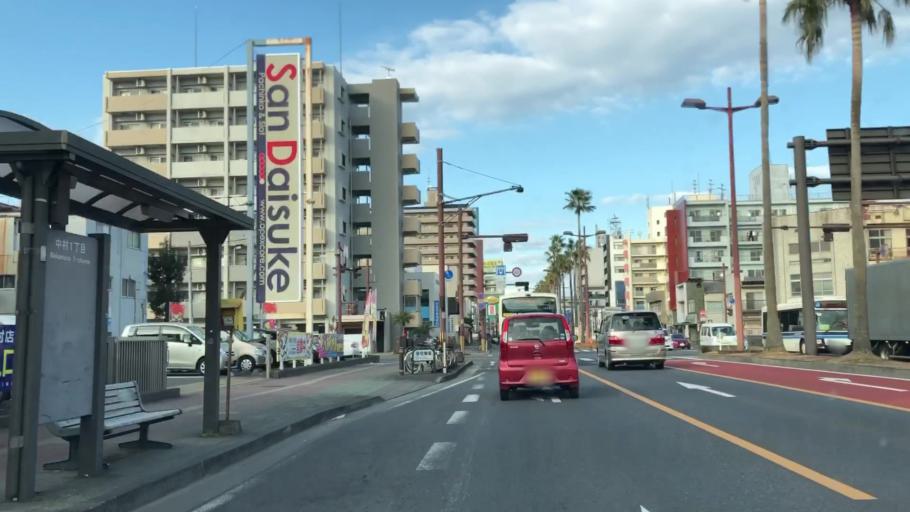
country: JP
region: Miyazaki
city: Miyazaki-shi
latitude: 31.9007
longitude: 131.4186
